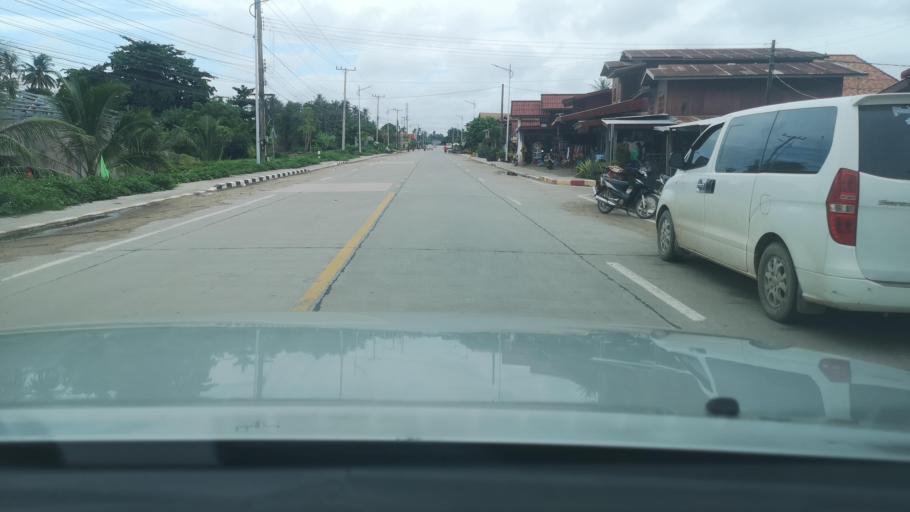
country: TH
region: Nong Khai
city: Tha Bo
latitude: 17.8155
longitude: 102.6653
